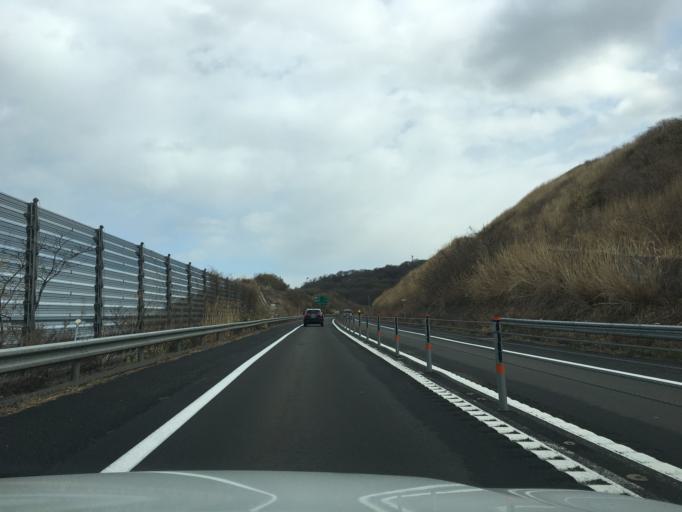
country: JP
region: Yamagata
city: Yuza
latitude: 39.3130
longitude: 139.9858
